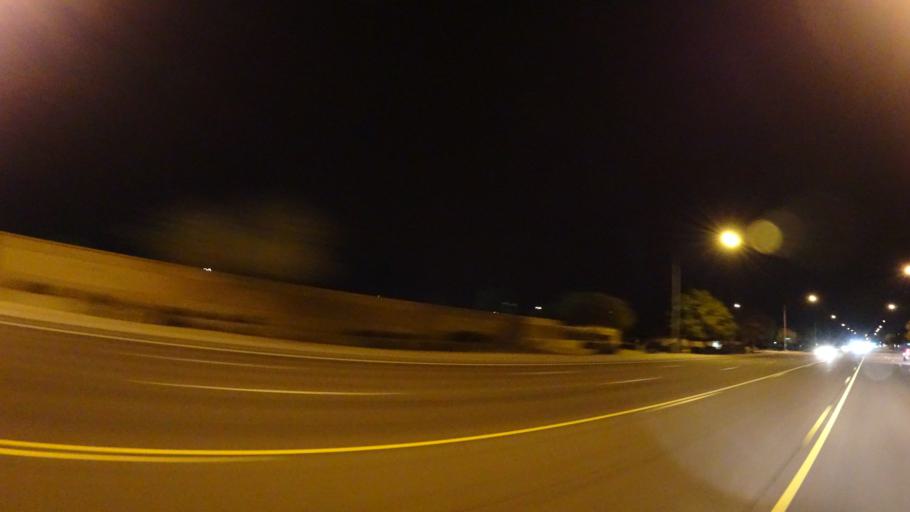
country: US
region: Arizona
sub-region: Maricopa County
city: Gilbert
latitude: 33.3939
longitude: -111.7113
